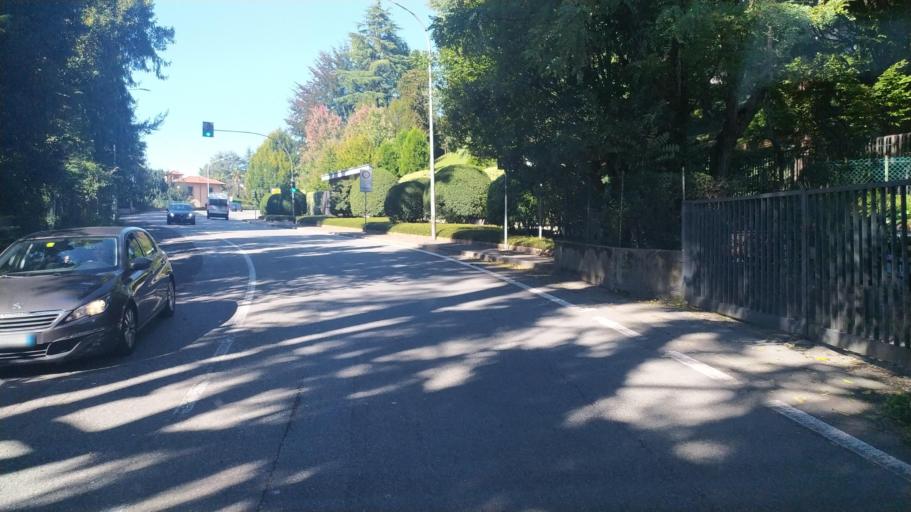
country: IT
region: Lombardy
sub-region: Provincia di Varese
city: Gazzada Schianno
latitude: 45.7970
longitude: 8.8347
